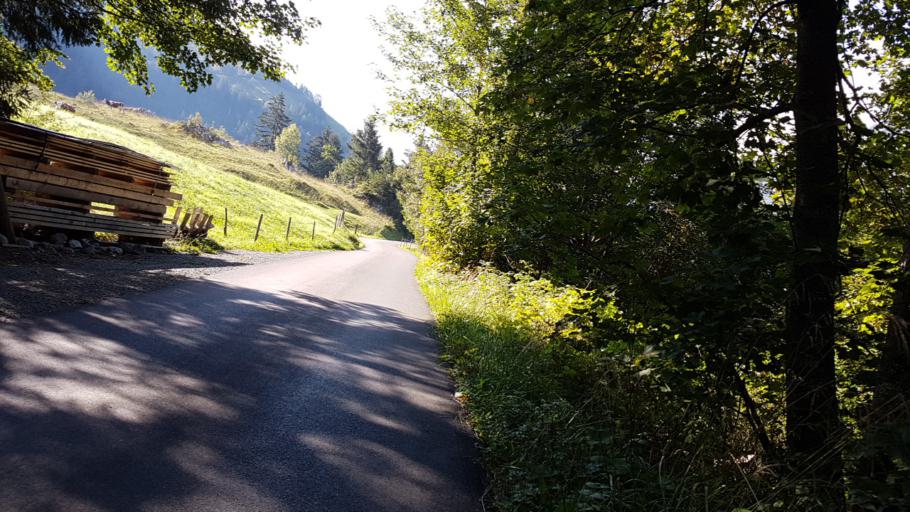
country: CH
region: Bern
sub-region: Frutigen-Niedersimmental District
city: Frutigen
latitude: 46.5533
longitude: 7.6705
